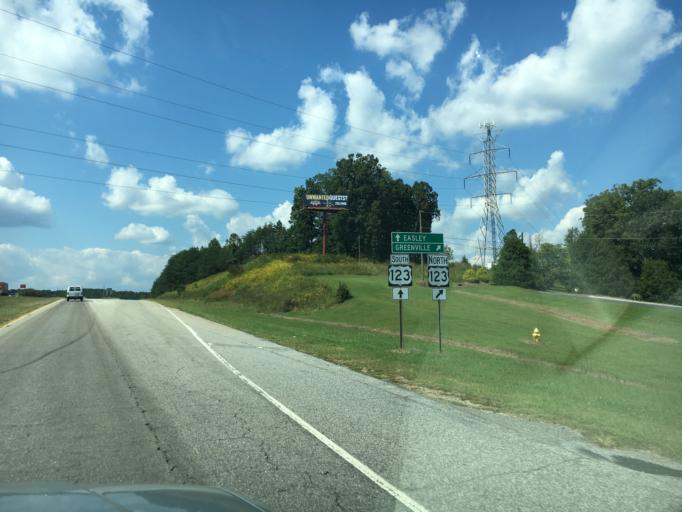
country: US
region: South Carolina
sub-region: Anderson County
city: Powdersville
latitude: 34.8237
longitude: -82.5244
